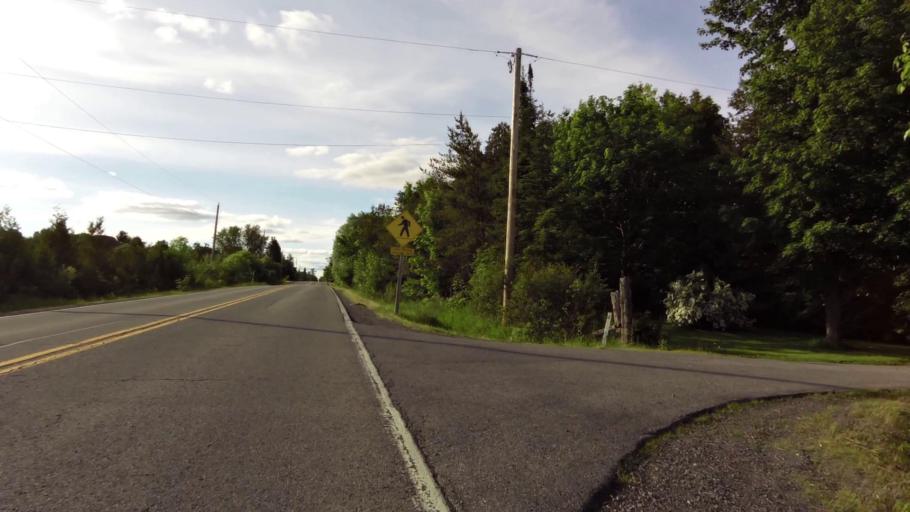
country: CA
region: Ontario
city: Ottawa
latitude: 45.2324
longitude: -75.6098
